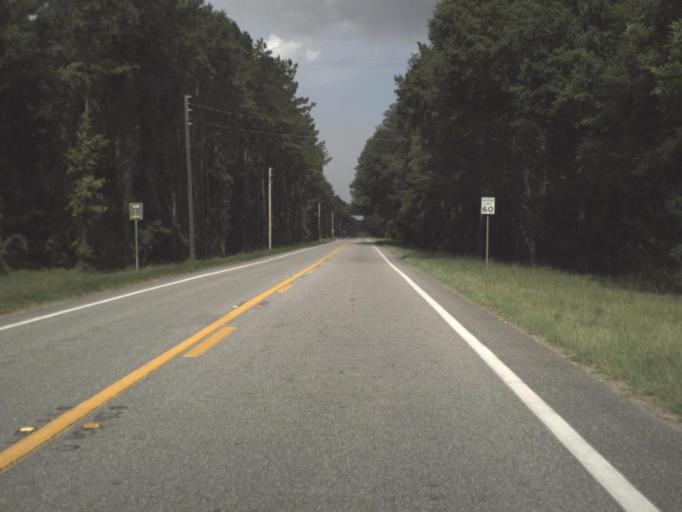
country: US
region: Florida
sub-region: Suwannee County
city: Live Oak
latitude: 30.3910
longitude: -83.1846
